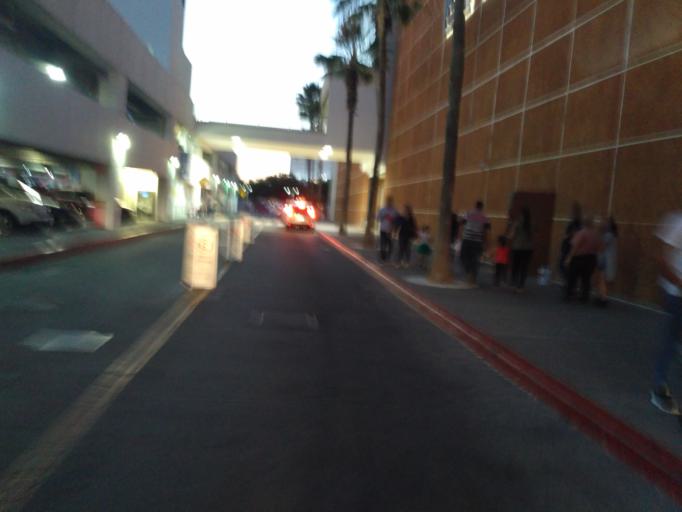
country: MX
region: Sinaloa
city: Culiacan
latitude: 24.8148
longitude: -107.4019
